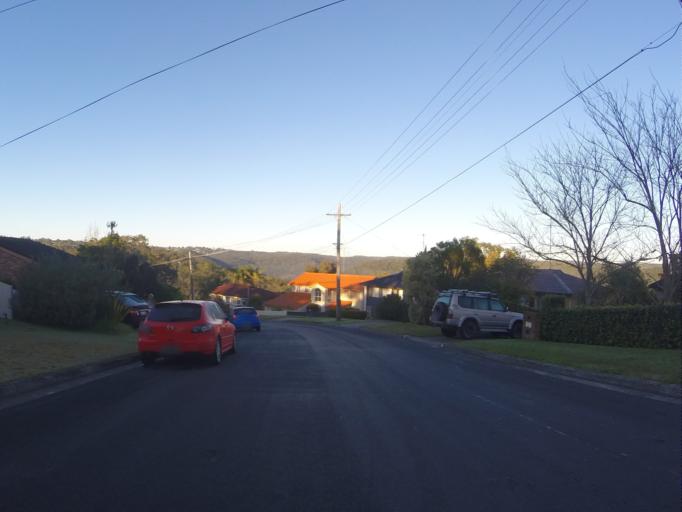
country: AU
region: New South Wales
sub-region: Sutherland Shire
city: Engadine
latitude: -34.0706
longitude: 151.0002
